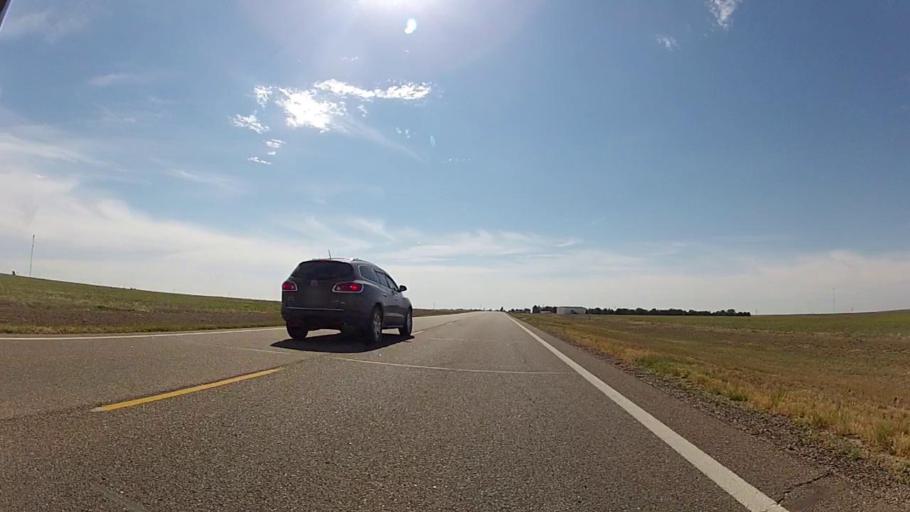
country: US
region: Kansas
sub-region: Grant County
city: Ulysses
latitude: 37.5659
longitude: -101.3153
